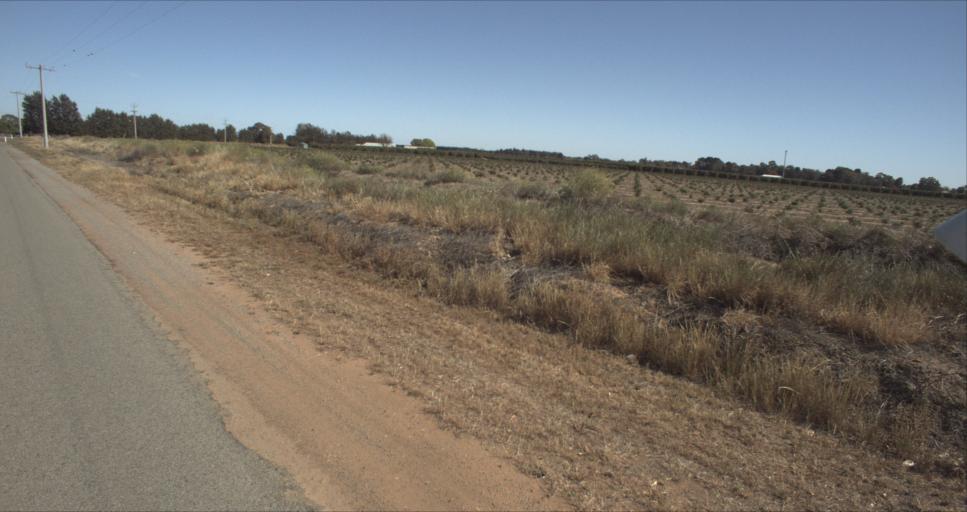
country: AU
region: New South Wales
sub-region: Leeton
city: Leeton
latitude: -34.5393
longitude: 146.3375
